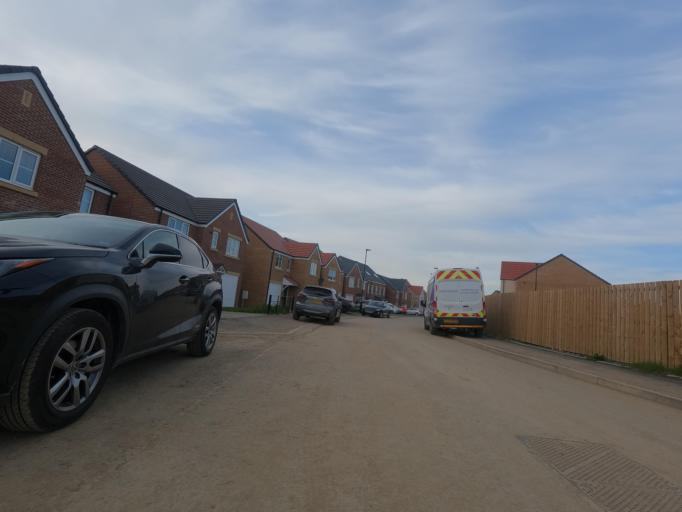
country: GB
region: England
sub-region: Newcastle upon Tyne
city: Dinnington
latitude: 55.0521
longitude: -1.6813
